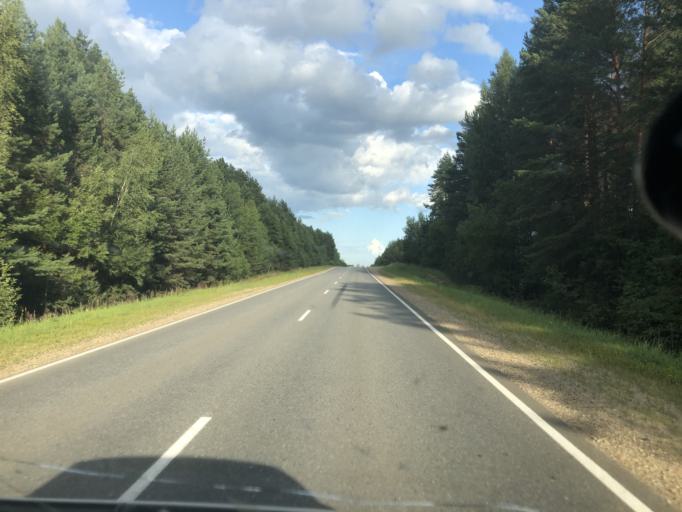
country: RU
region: Kaluga
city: Yukhnov
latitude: 54.7103
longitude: 35.2535
